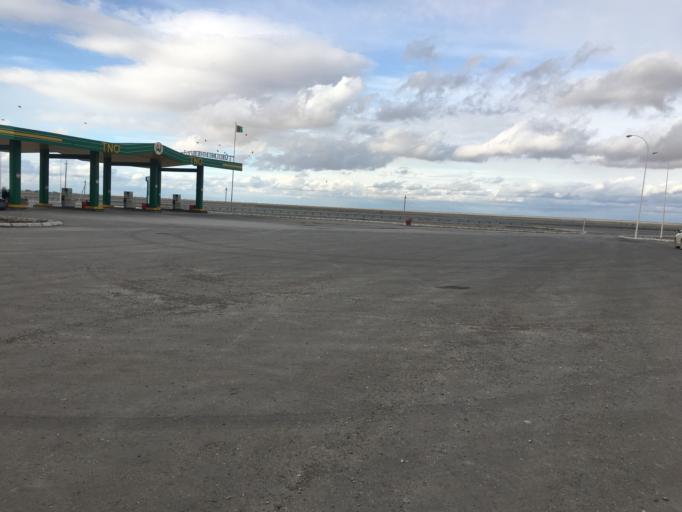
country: TM
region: Balkan
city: Serdar
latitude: 38.9735
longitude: 56.3178
